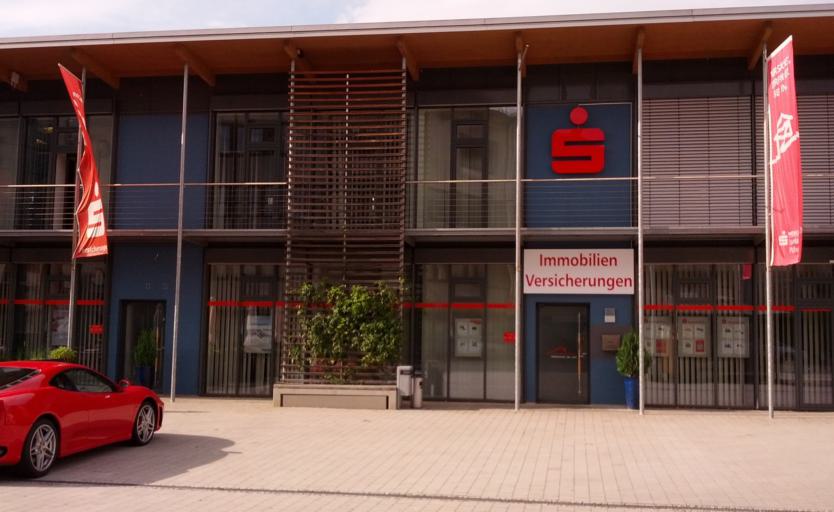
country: DE
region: Bavaria
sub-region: Upper Bavaria
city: Pfaffenhofen an der Ilm
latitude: 48.5290
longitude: 11.5105
